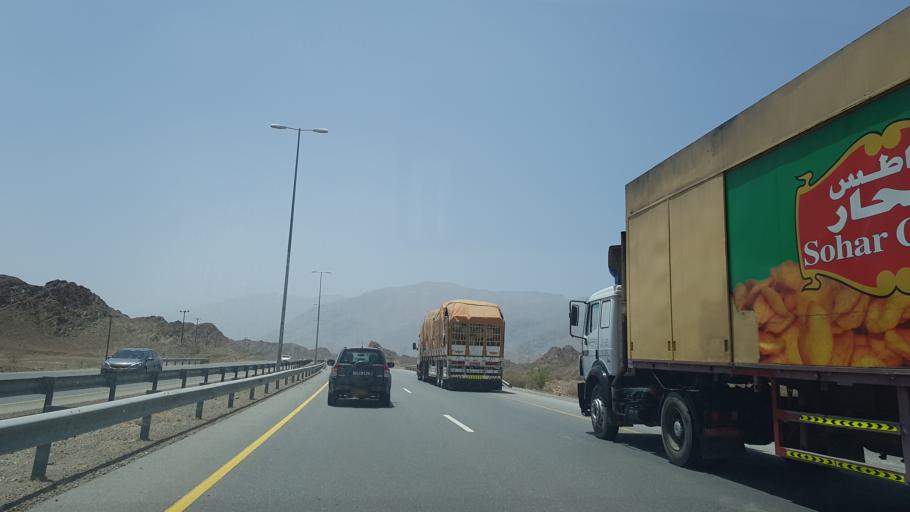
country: OM
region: Muhafazat ad Dakhiliyah
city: Sufalat Sama'il
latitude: 23.3354
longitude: 57.9852
